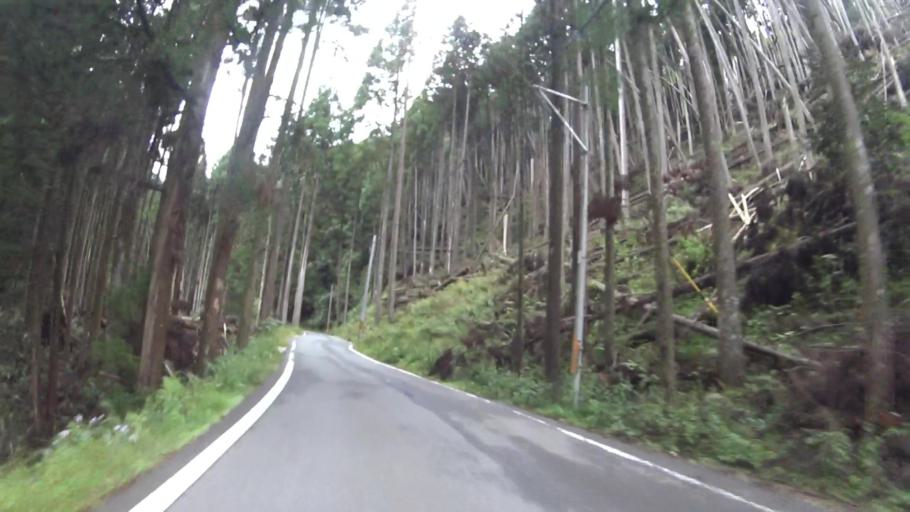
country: JP
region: Kyoto
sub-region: Kyoto-shi
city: Kamigyo-ku
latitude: 35.1306
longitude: 135.7788
